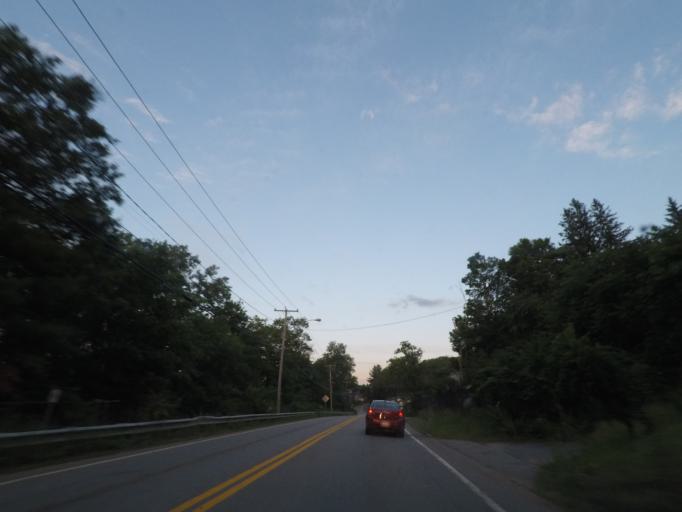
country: US
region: Massachusetts
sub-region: Worcester County
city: Southbridge
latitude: 42.0649
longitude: -72.0091
